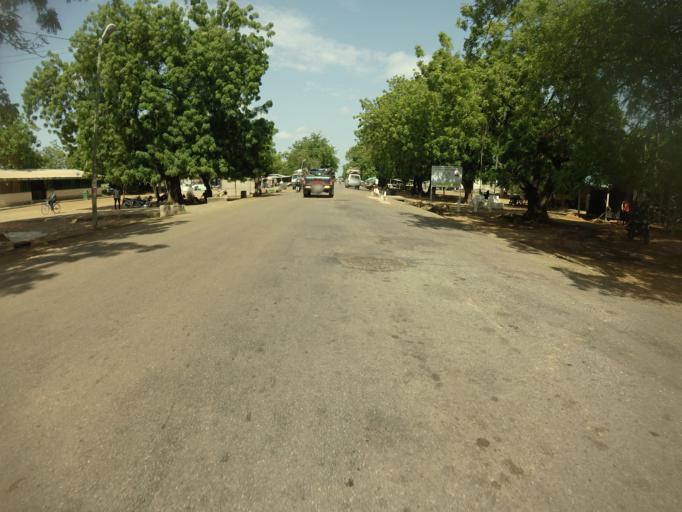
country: GH
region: Upper East
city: Bawku
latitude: 11.0685
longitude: -0.2008
